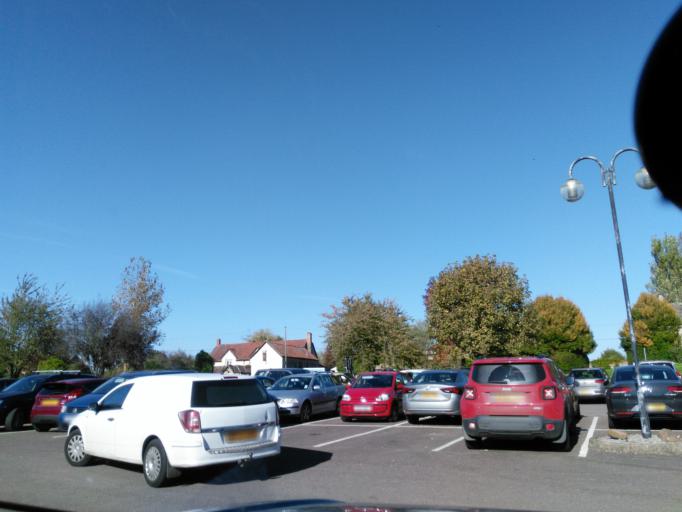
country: GB
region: England
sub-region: Wiltshire
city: Atworth
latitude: 51.3905
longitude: -2.1767
